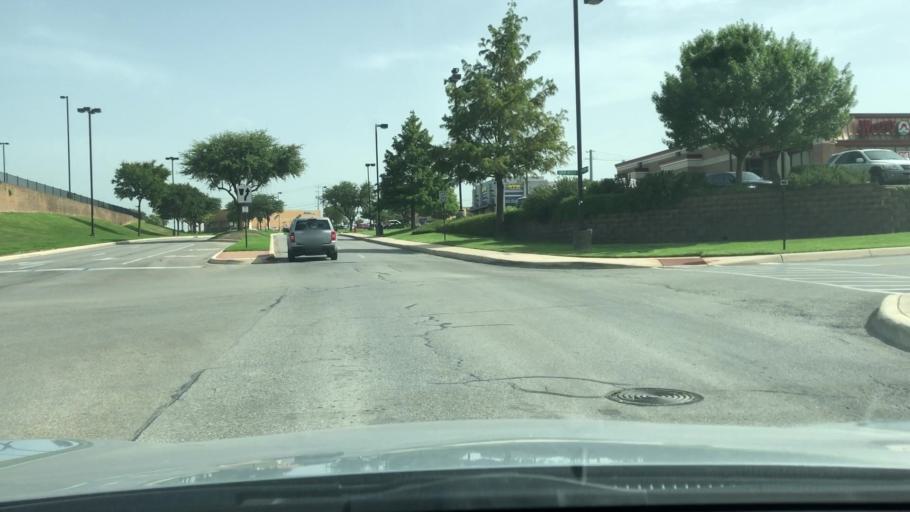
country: US
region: Texas
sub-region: Bexar County
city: Live Oak
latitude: 29.5677
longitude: -98.3300
